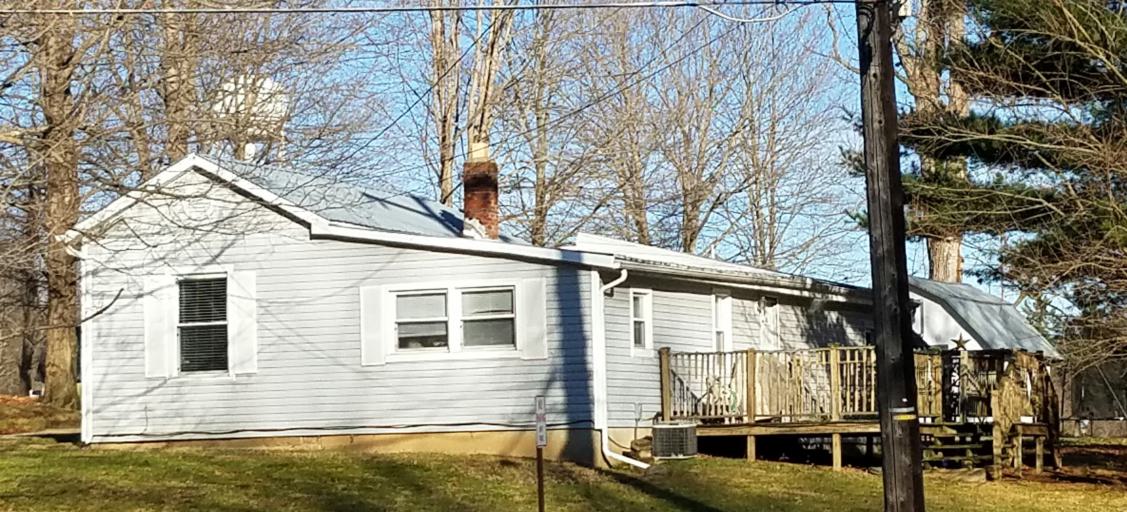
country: US
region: Ohio
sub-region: Morrow County
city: Mount Gilead
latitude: 40.5532
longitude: -82.8218
